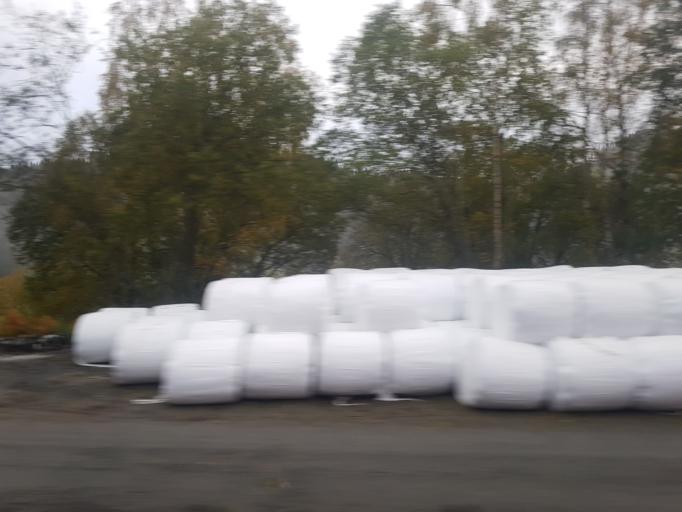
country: NO
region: Sor-Trondelag
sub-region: Midtre Gauldal
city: Storen
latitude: 62.9857
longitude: 10.2391
